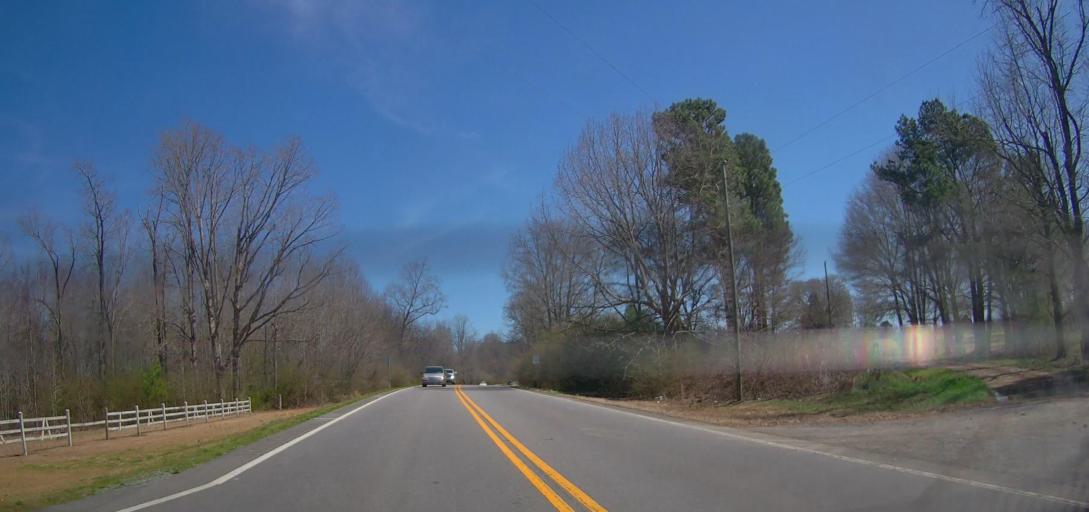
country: US
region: Alabama
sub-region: Blount County
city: Blountsville
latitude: 34.1734
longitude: -86.5330
